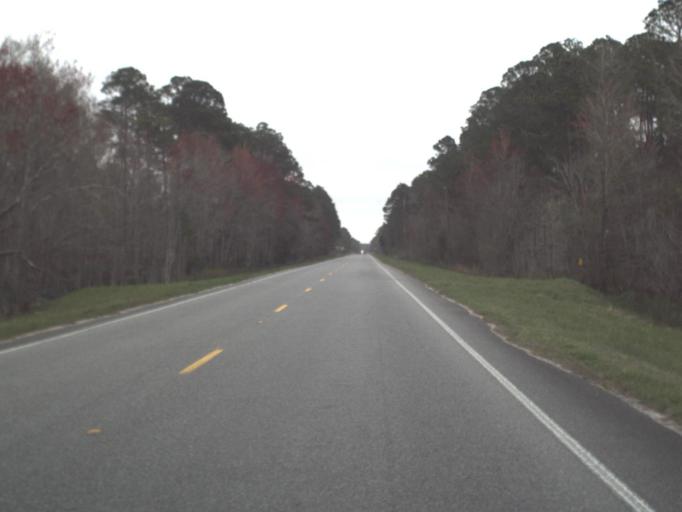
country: US
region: Florida
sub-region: Leon County
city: Woodville
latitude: 30.1913
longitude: -84.0811
